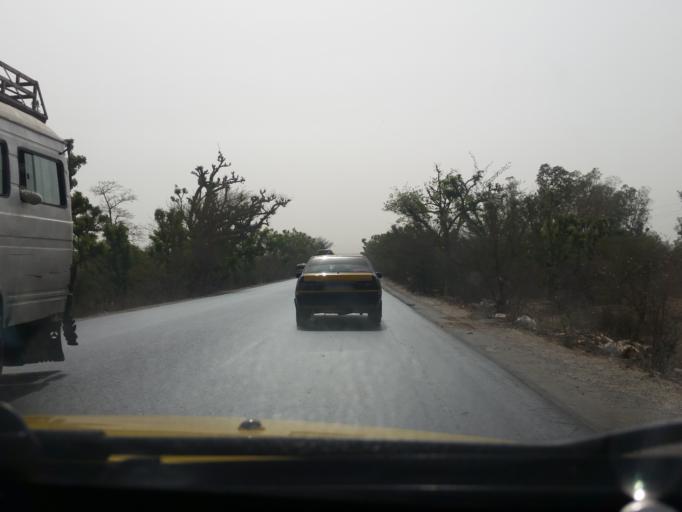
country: SN
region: Thies
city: Pout
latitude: 14.7623
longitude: -17.0306
